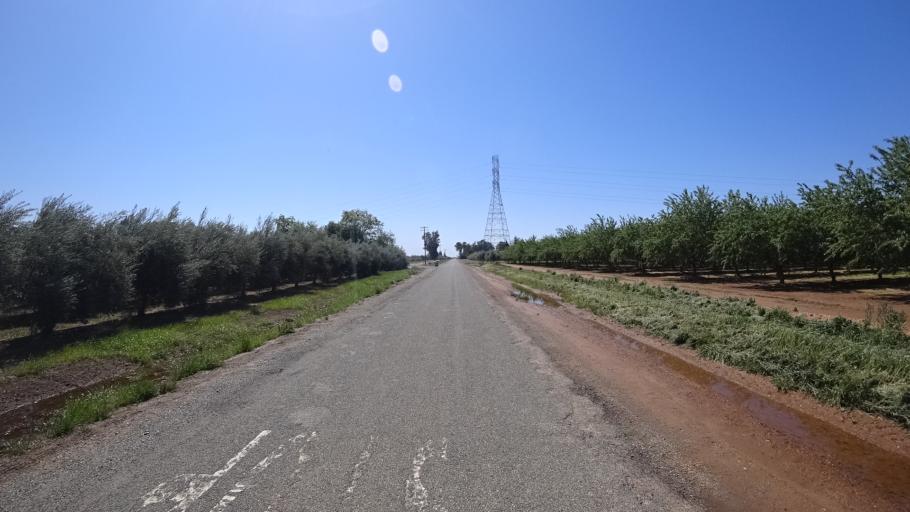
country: US
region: California
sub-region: Glenn County
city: Orland
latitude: 39.7953
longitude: -122.1691
